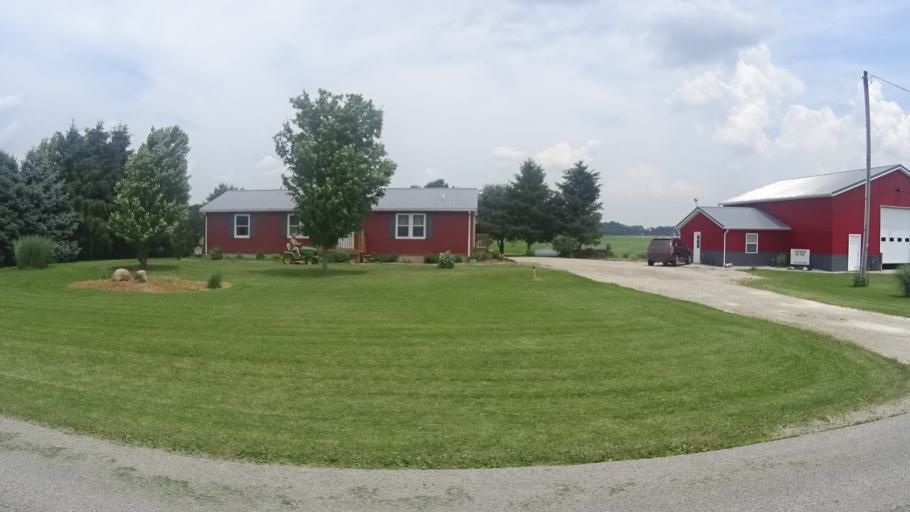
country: US
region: Ohio
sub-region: Erie County
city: Milan
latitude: 41.3028
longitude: -82.6547
